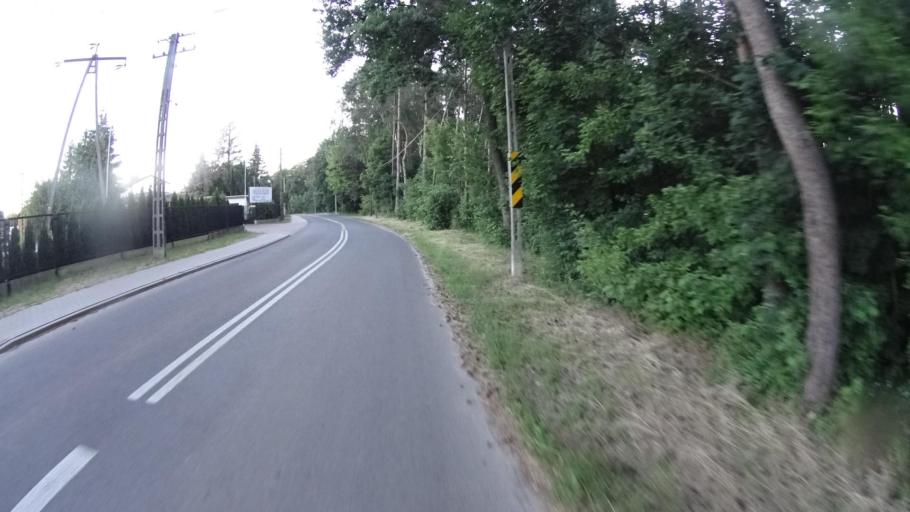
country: PL
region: Masovian Voivodeship
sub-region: Powiat warszawski zachodni
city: Jozefow
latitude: 52.2678
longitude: 20.6874
